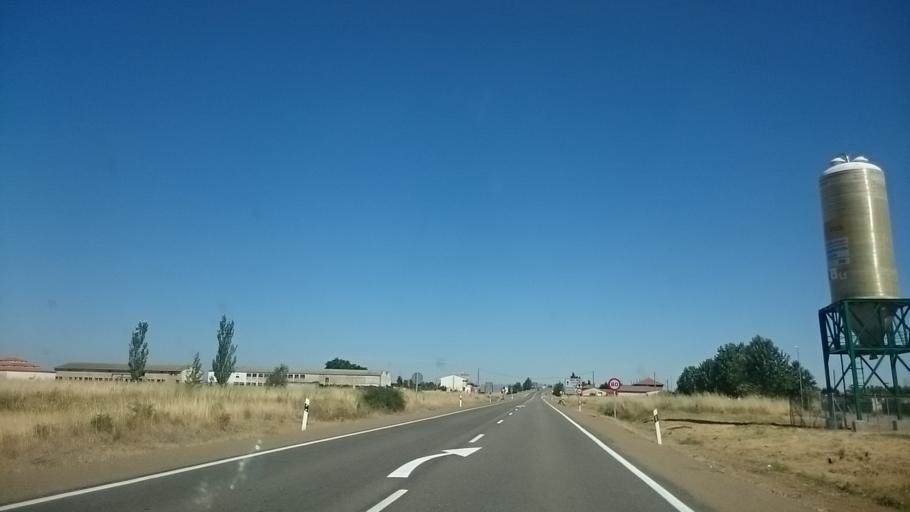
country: ES
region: Castille and Leon
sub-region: Provincia de Leon
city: Santas Martas
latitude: 42.4555
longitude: -5.3870
